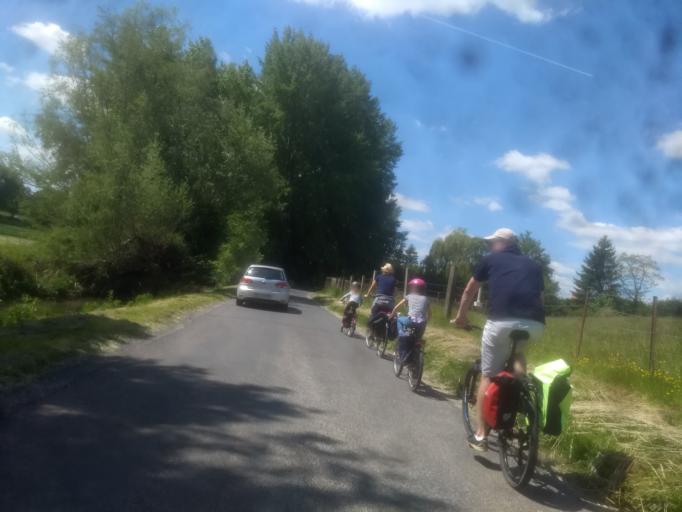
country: FR
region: Nord-Pas-de-Calais
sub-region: Departement du Pas-de-Calais
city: Riviere
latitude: 50.2405
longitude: 2.7054
